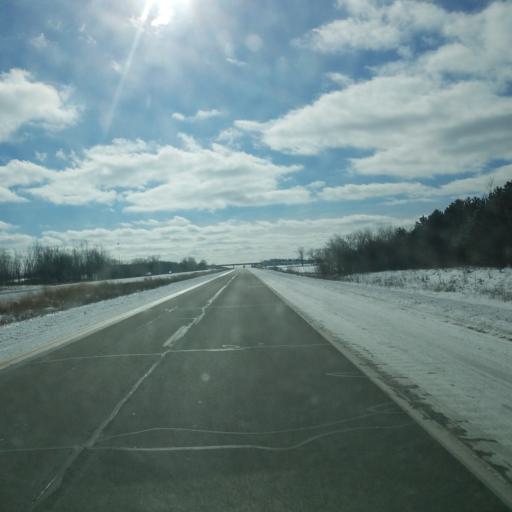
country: US
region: Michigan
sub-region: Clinton County
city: Saint Johns
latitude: 42.9515
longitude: -84.5189
